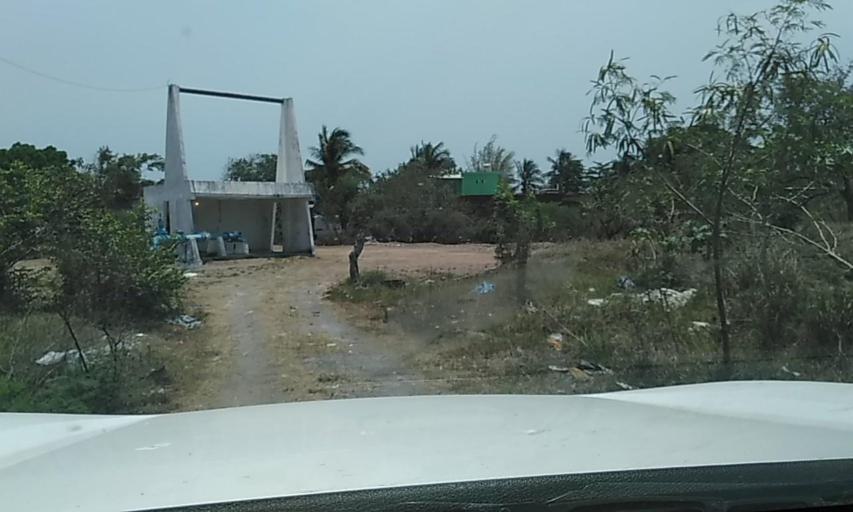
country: MX
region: Veracruz
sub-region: Veracruz
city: Las Amapolas
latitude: 19.1536
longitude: -96.2005
